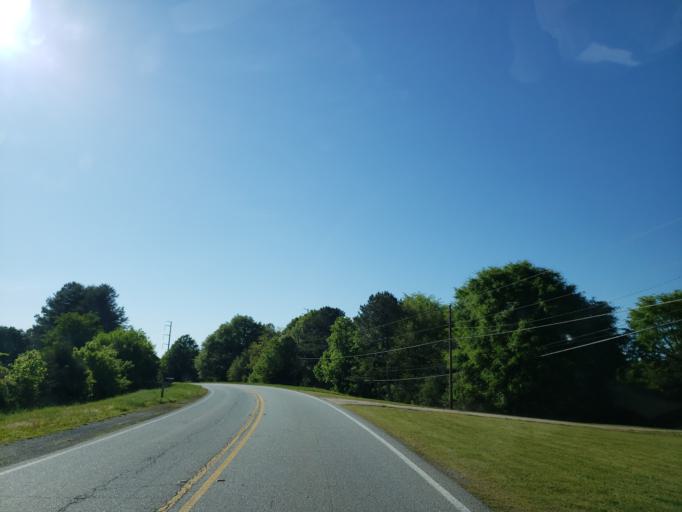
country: US
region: Georgia
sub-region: Polk County
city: Cedartown
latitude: 34.0011
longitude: -85.2386
